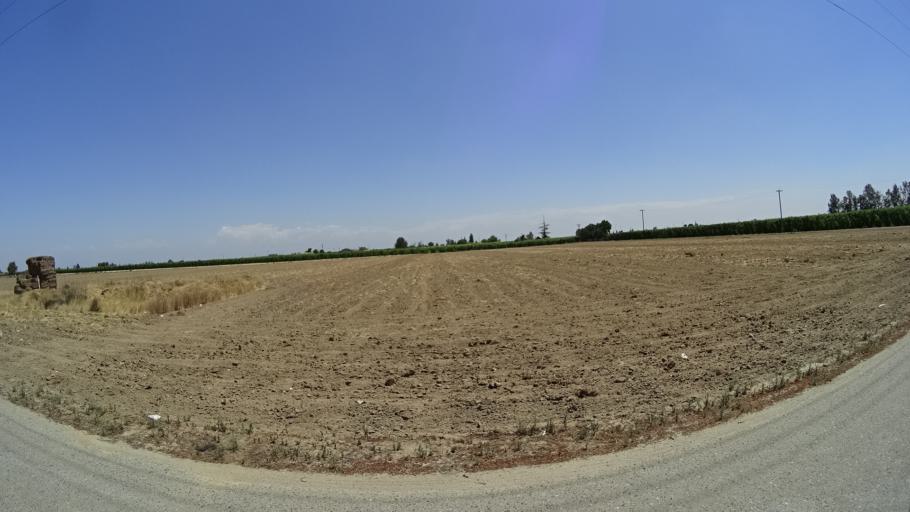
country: US
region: California
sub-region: Fresno County
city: Kingsburg
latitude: 36.4749
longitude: -119.5913
